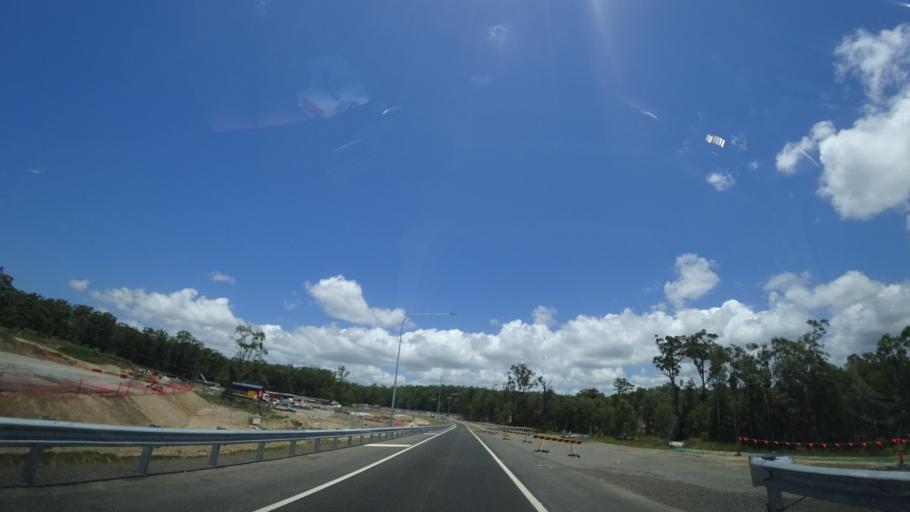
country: AU
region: Queensland
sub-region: Sunshine Coast
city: Little Mountain
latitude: -26.7746
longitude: 153.0453
